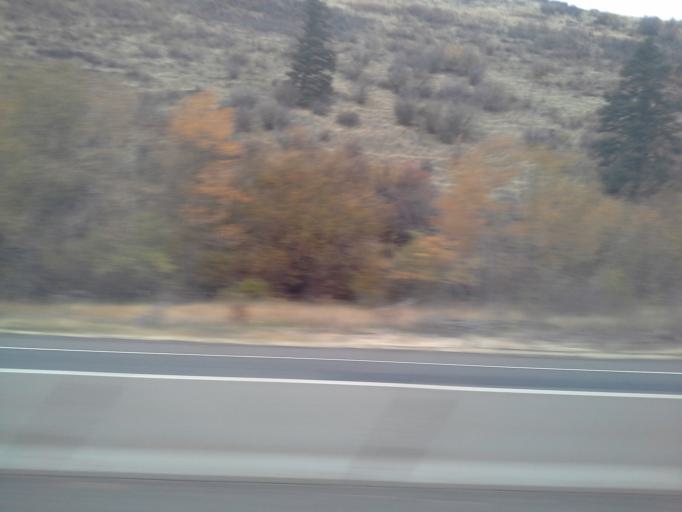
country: US
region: Oregon
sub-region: Union County
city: La Grande
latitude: 45.2263
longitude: -118.0124
